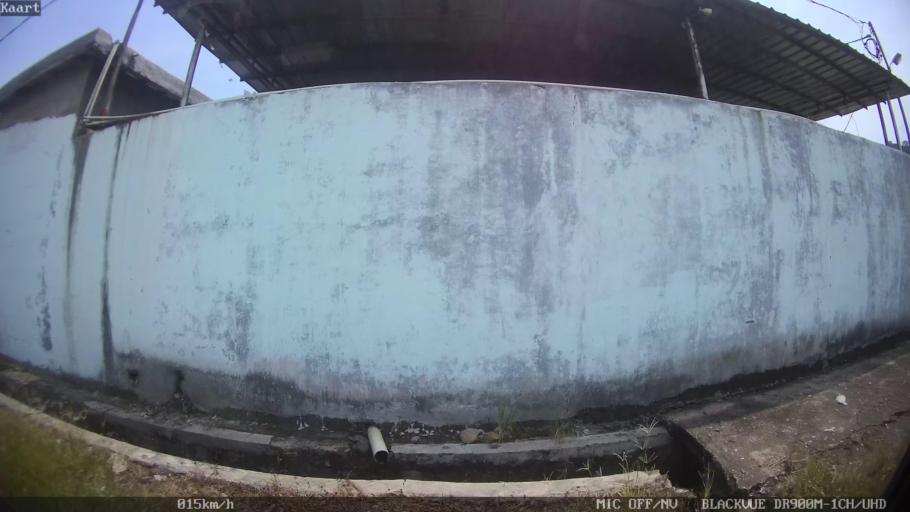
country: ID
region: Lampung
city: Bandarlampung
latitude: -5.4587
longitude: 105.2478
